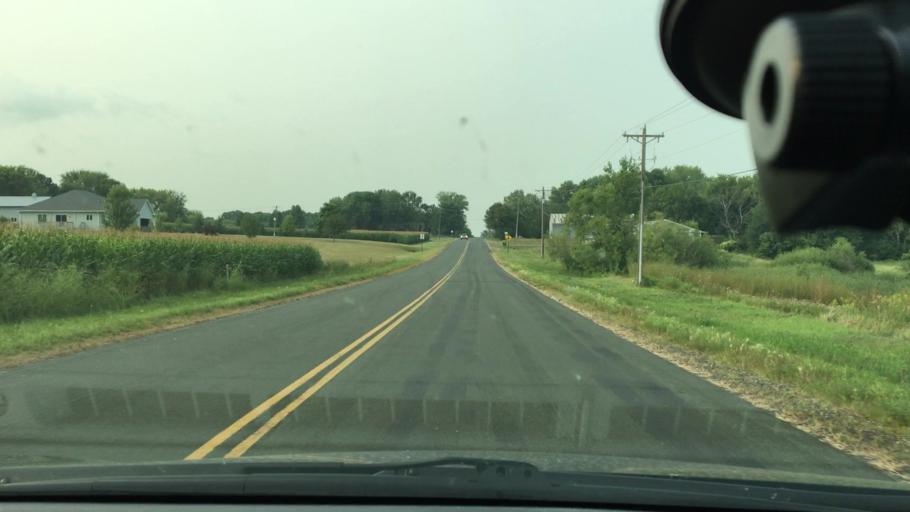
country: US
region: Minnesota
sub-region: Wright County
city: Albertville
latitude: 45.2876
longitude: -93.6839
